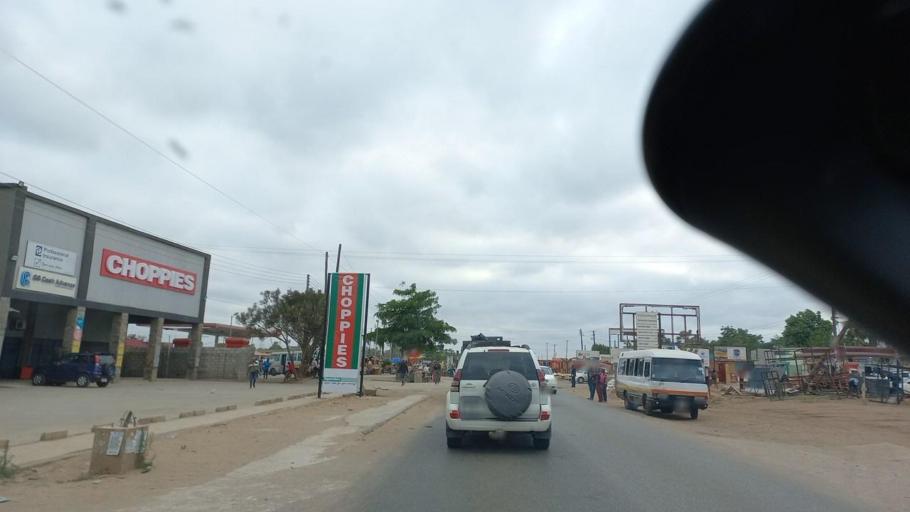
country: ZM
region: Lusaka
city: Chongwe
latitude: -15.3324
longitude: 28.6738
